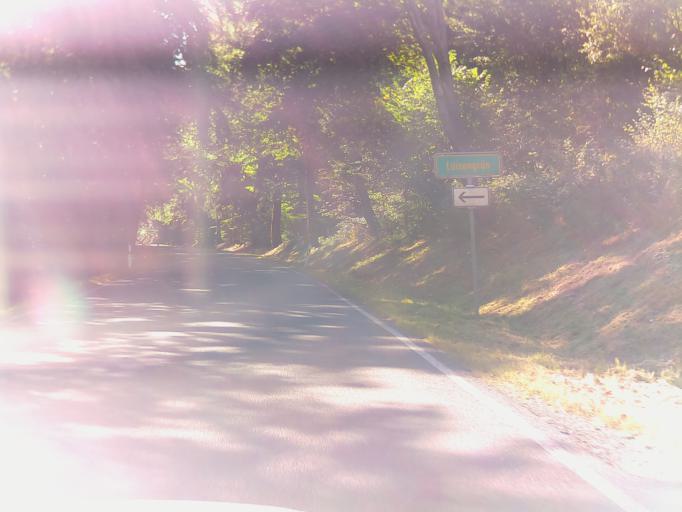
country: DE
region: Thuringia
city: Wurzbach
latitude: 50.4822
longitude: 11.4714
